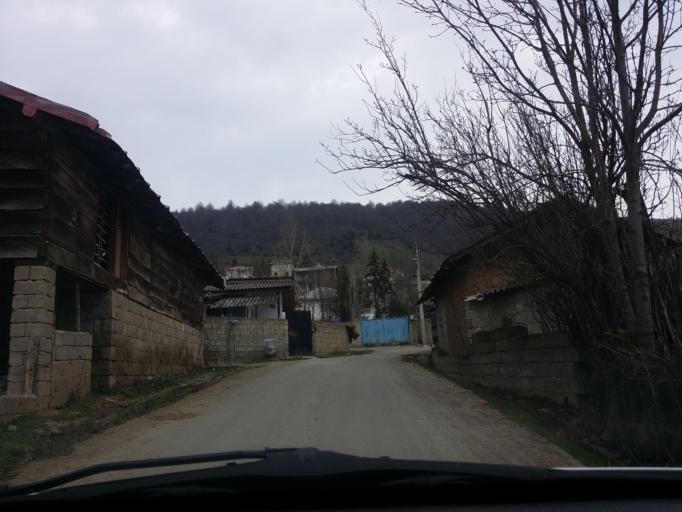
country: IR
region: Mazandaran
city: `Abbasabad
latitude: 36.5489
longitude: 51.1648
